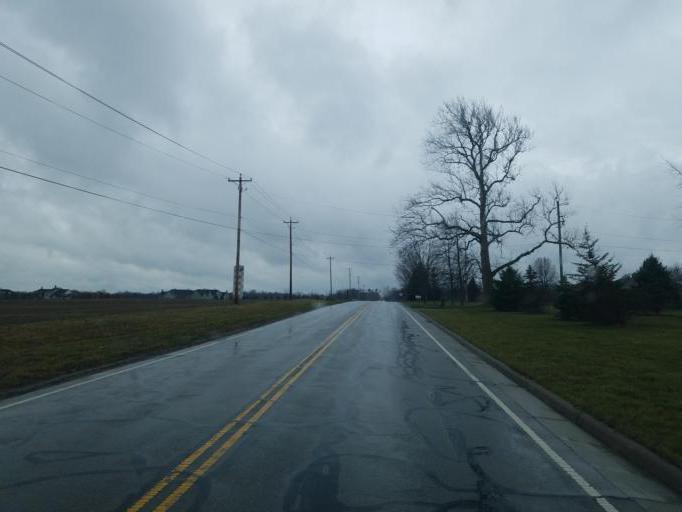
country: US
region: Ohio
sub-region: Delaware County
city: Sunbury
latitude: 40.2786
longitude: -82.9079
